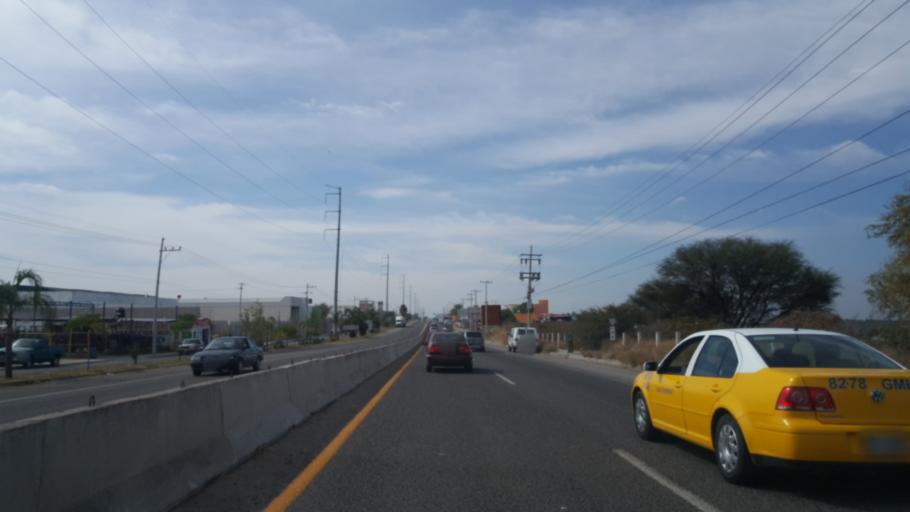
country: MX
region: Jalisco
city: San Juan de los Lagos
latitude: 21.2788
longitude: -102.2951
